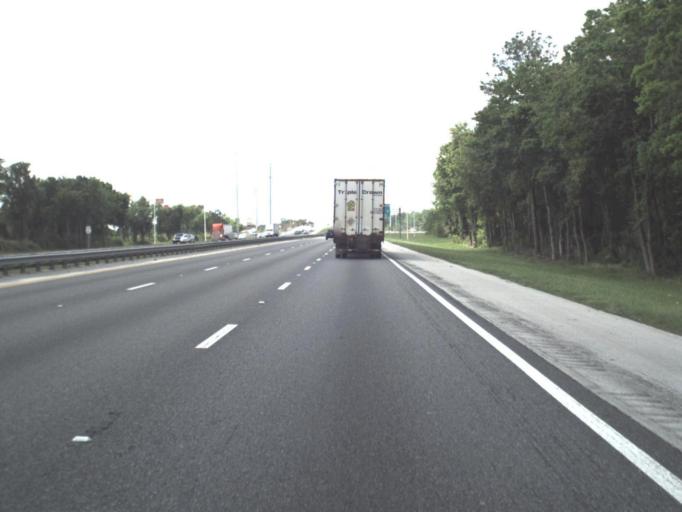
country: US
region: Florida
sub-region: Saint Johns County
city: Saint Augustine
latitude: 29.9104
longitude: -81.4097
